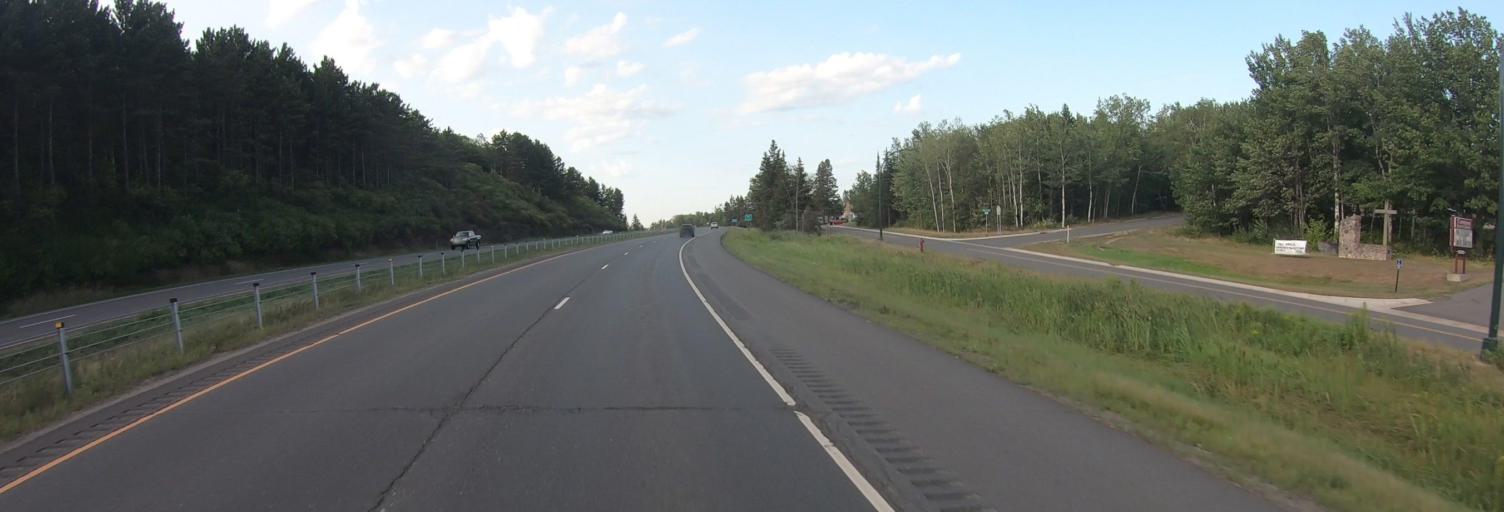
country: US
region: Minnesota
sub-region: Saint Louis County
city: Eveleth
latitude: 47.4868
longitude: -92.5305
